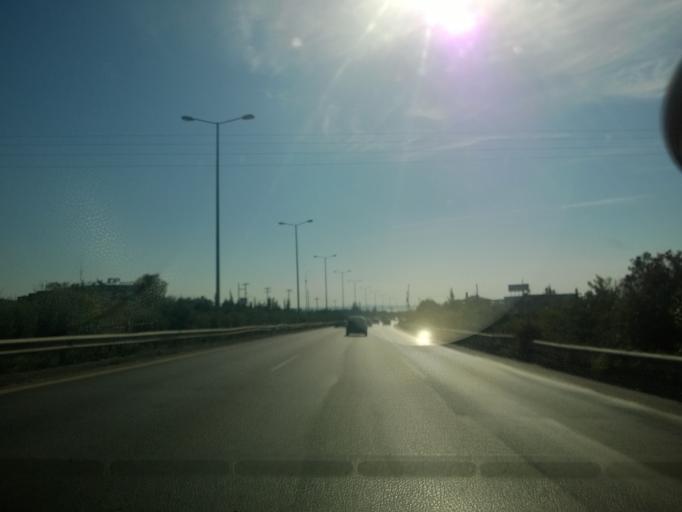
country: GR
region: Central Macedonia
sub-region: Nomos Thessalonikis
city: Pylaia
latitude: 40.5944
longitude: 22.9942
